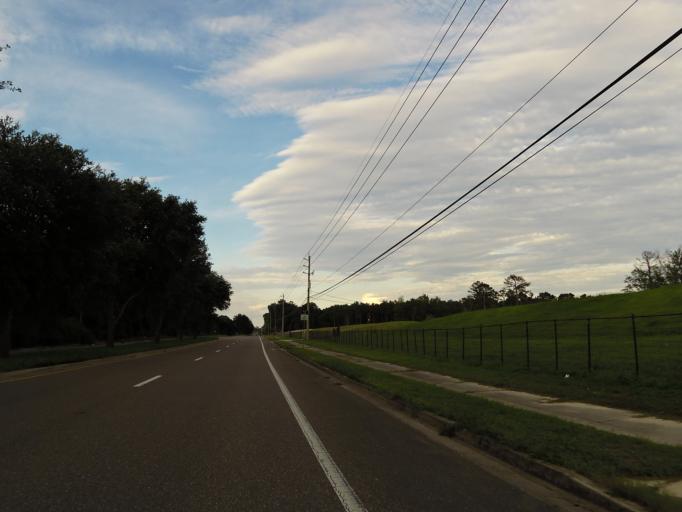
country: US
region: Florida
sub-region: Nassau County
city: Nassau Village-Ratliff
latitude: 30.3716
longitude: -81.7991
